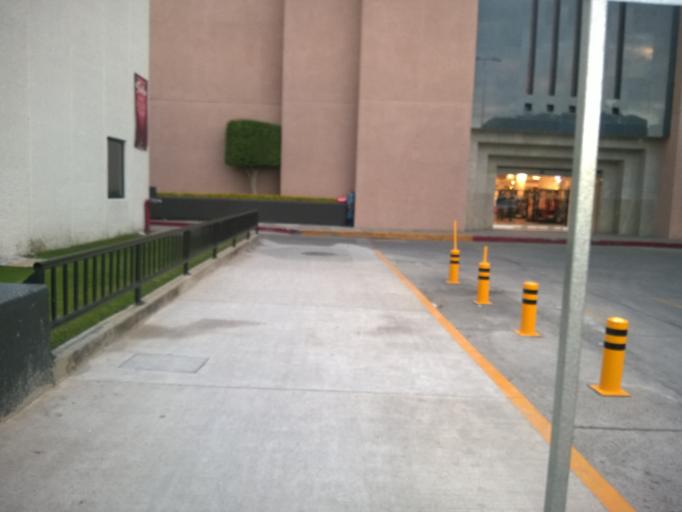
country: MX
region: Guanajuato
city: Leon
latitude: 21.1582
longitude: -101.6944
